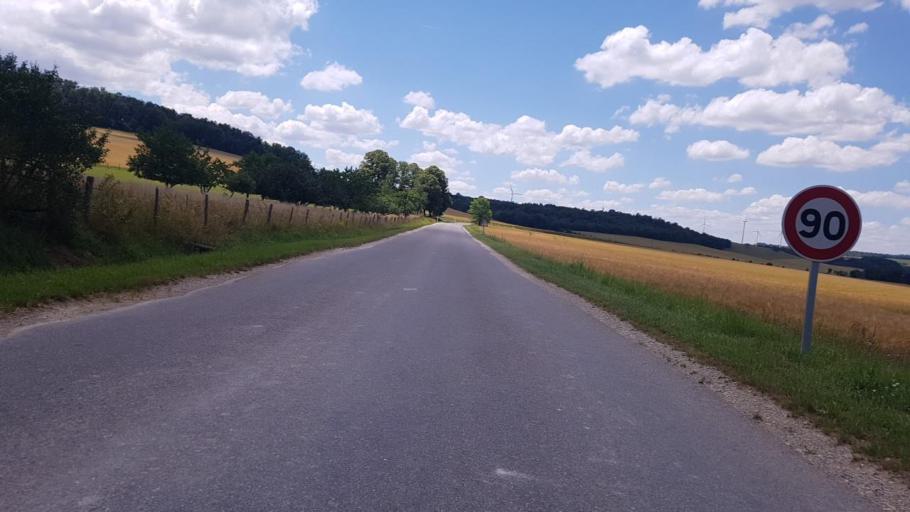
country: FR
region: Lorraine
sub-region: Departement de la Meuse
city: Vacon
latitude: 48.6417
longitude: 5.5098
